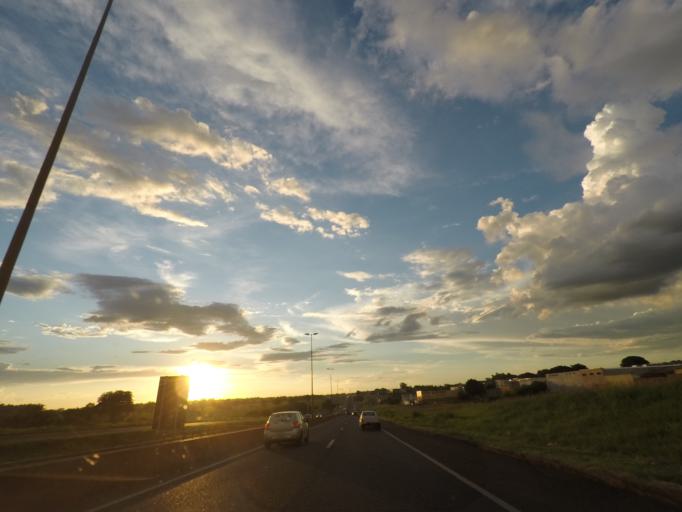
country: BR
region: Minas Gerais
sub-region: Uberaba
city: Uberaba
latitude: -19.7792
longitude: -47.9497
